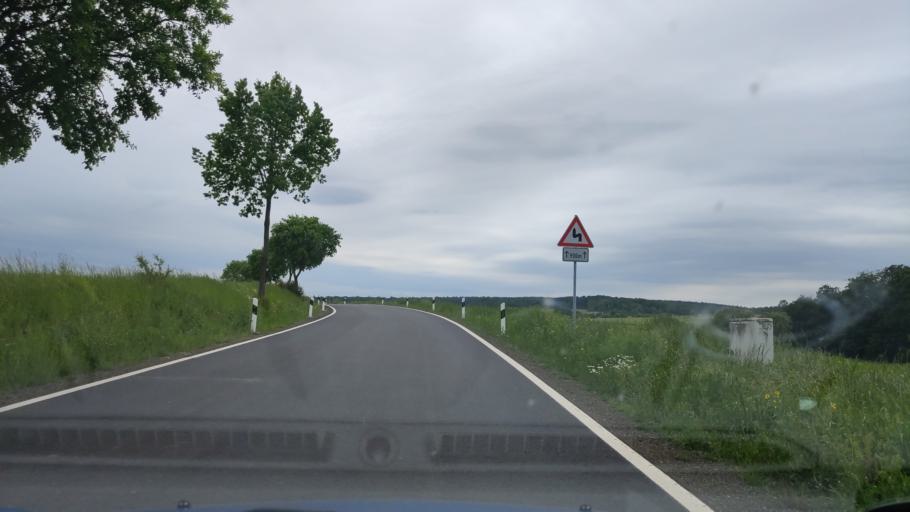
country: DE
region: Lower Saxony
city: Hardegsen
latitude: 51.7092
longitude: 9.7836
